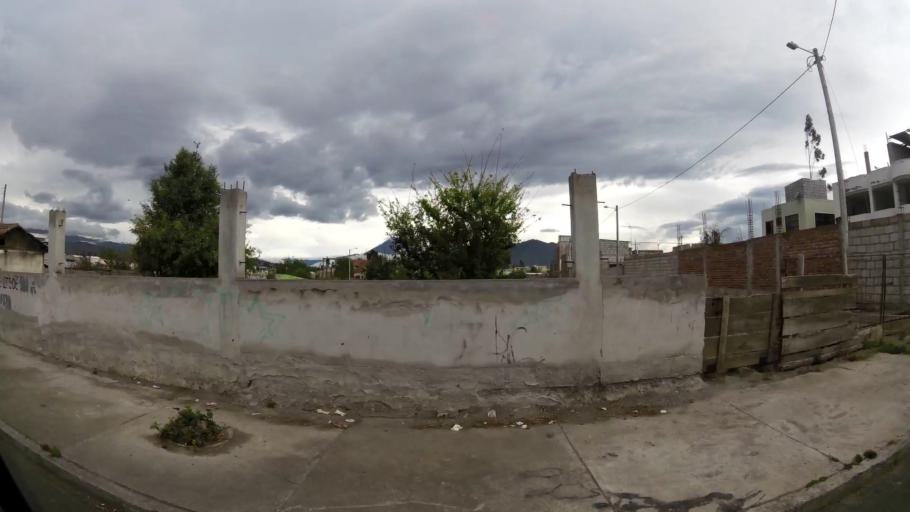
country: EC
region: Tungurahua
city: Ambato
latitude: -1.2774
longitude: -78.6232
